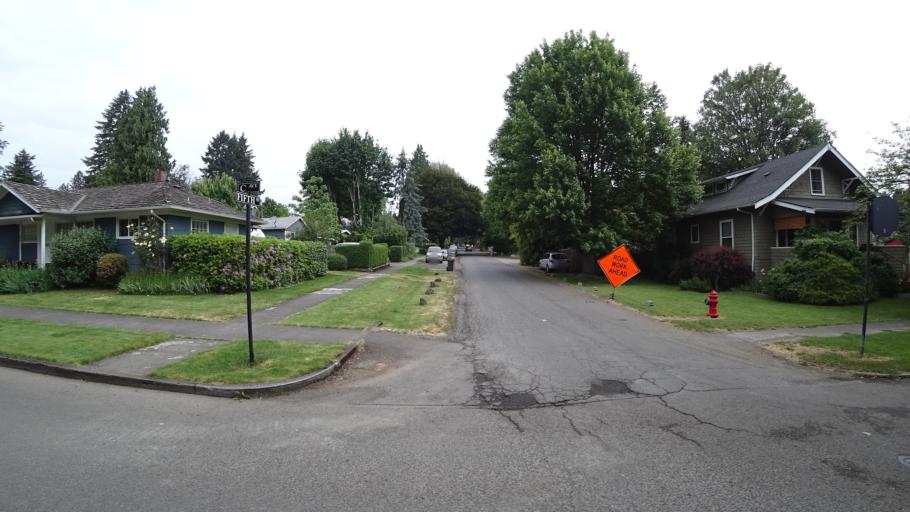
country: US
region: Oregon
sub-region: Clackamas County
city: Lake Oswego
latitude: 45.4224
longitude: -122.6687
